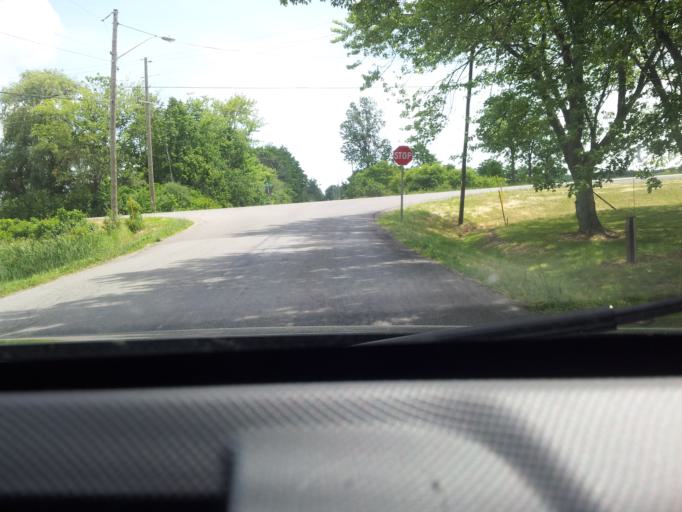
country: CA
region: Ontario
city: Norfolk County
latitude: 42.8284
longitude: -80.2555
